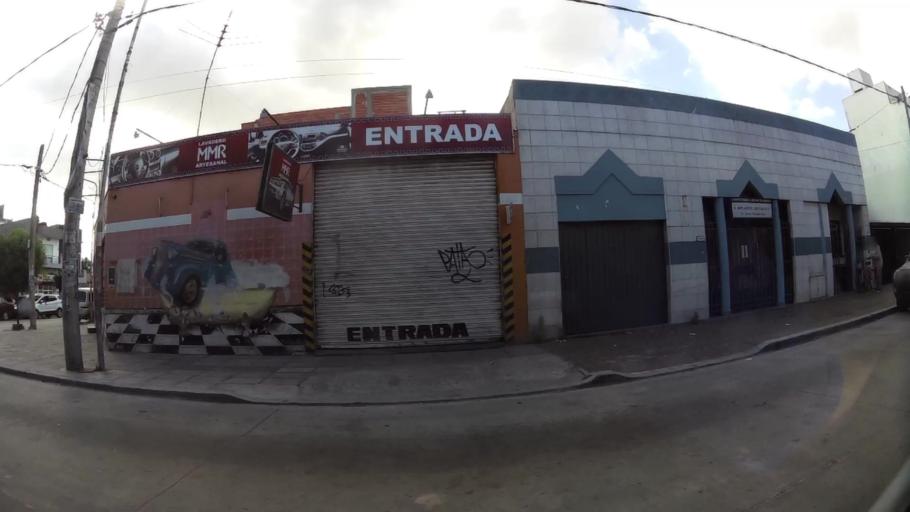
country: AR
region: Buenos Aires
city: San Justo
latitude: -34.6734
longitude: -58.5735
